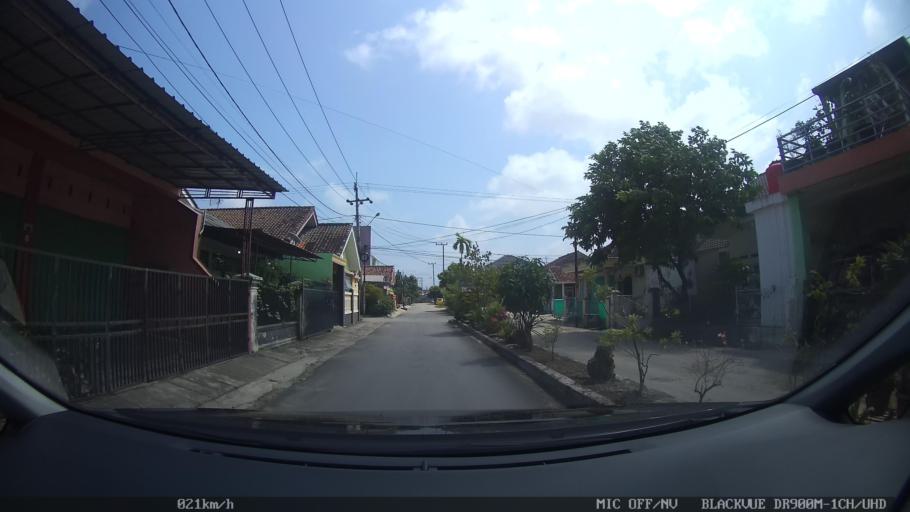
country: ID
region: Lampung
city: Kedaton
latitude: -5.3583
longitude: 105.2810
